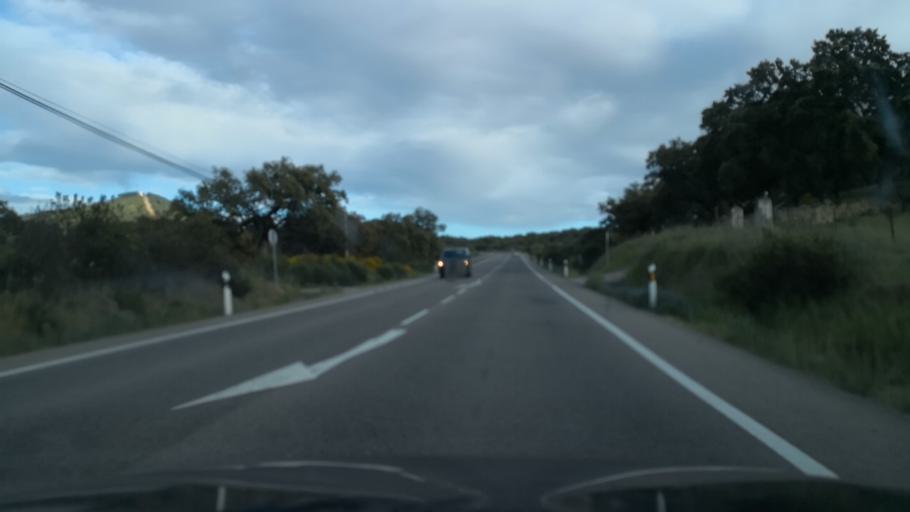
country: ES
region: Extremadura
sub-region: Provincia de Caceres
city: Pedroso de Acim
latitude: 39.8300
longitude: -6.3817
